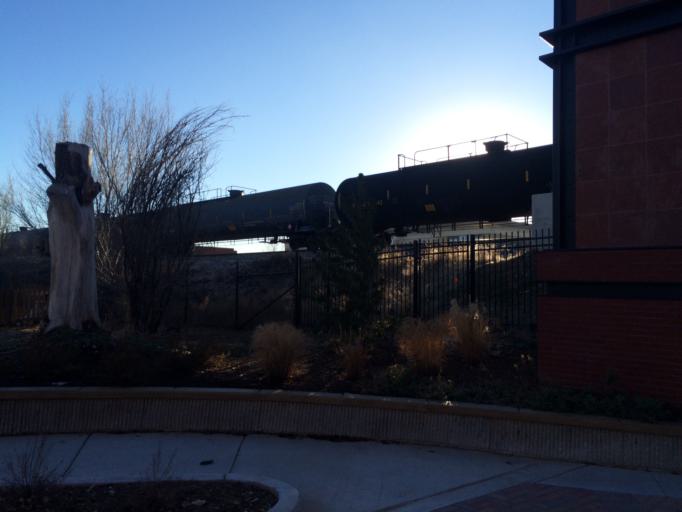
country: US
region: Colorado
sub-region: Boulder County
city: Louisville
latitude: 39.9797
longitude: -105.1302
